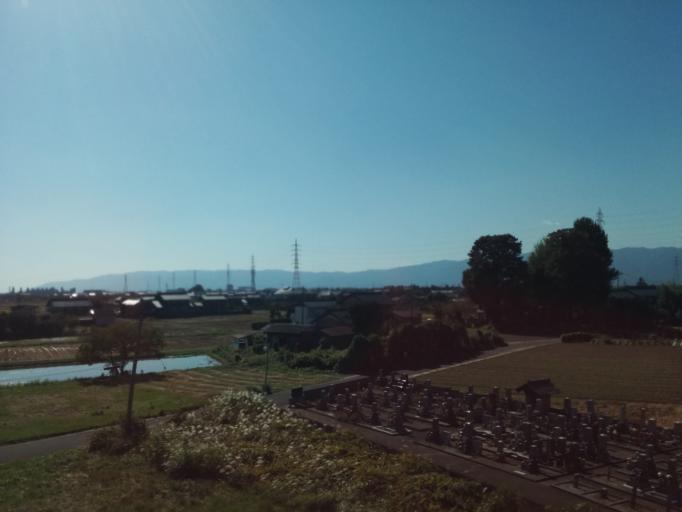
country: JP
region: Gifu
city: Ogaki
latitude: 35.3383
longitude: 136.6561
